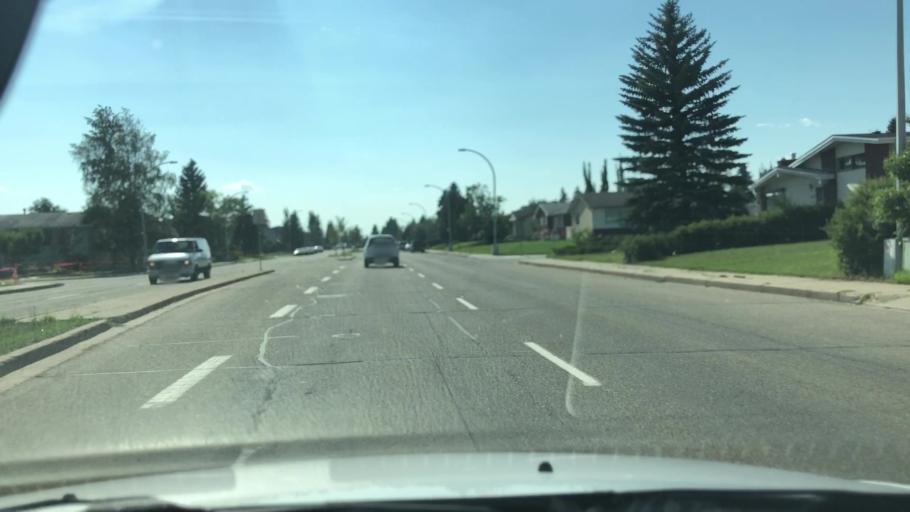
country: CA
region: Alberta
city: Edmonton
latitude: 53.6070
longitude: -113.4625
